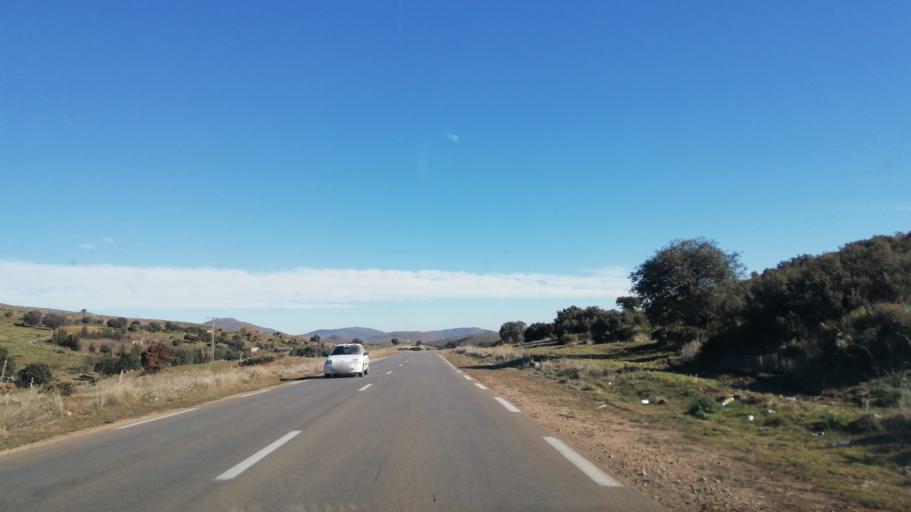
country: DZ
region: Tlemcen
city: Ouled Mimoun
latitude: 34.7542
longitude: -1.1535
